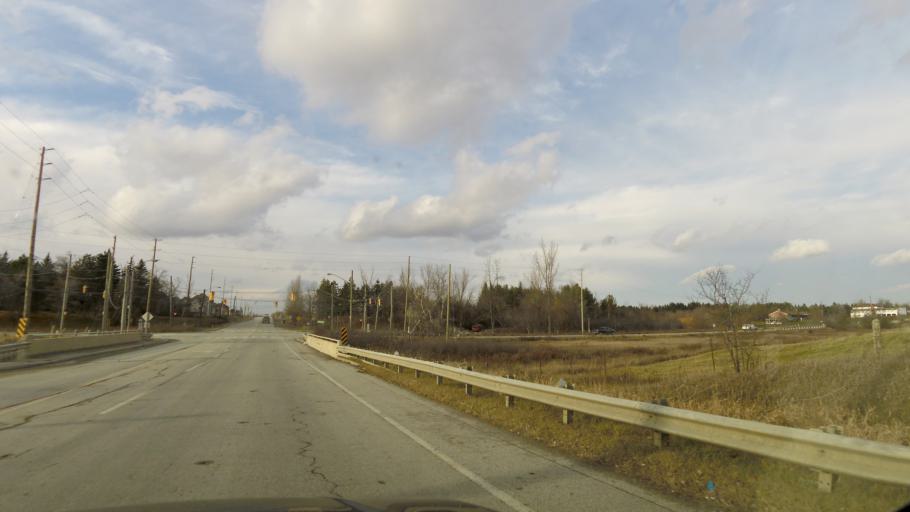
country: CA
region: Ontario
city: Brampton
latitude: 43.8111
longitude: -79.7159
